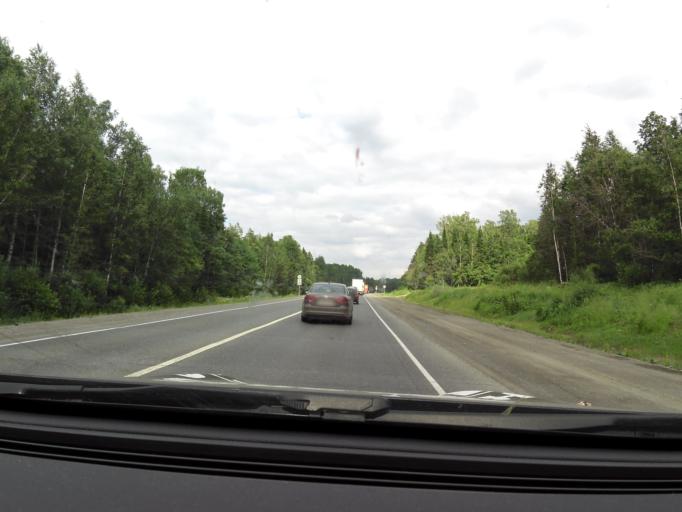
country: RU
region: Sverdlovsk
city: Bilimbay
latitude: 56.8573
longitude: 59.7126
